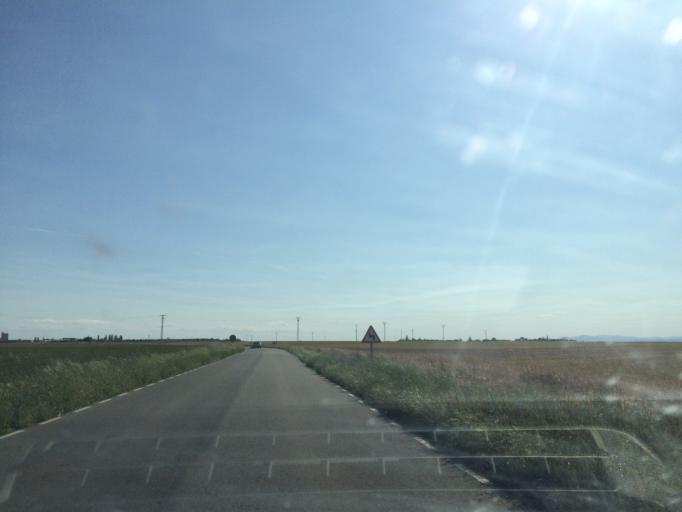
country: ES
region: Madrid
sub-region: Provincia de Madrid
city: Valdepielagos
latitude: 40.7189
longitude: -3.4192
